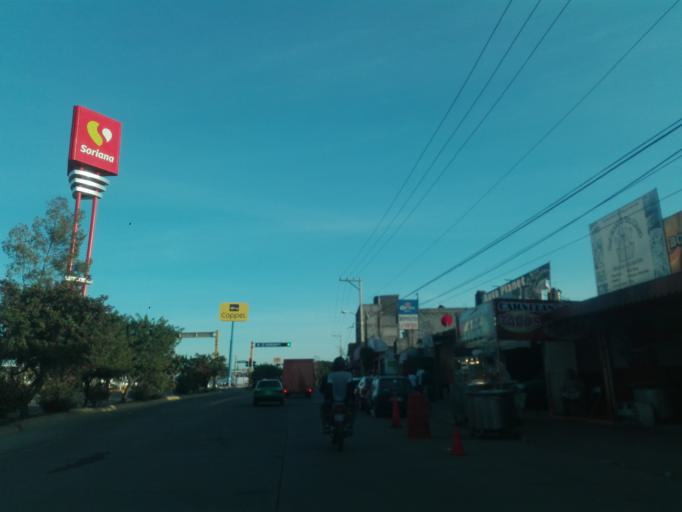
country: MX
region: Guanajuato
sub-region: Leon
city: San Jose de Duran (Los Troncoso)
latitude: 21.0833
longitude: -101.6426
